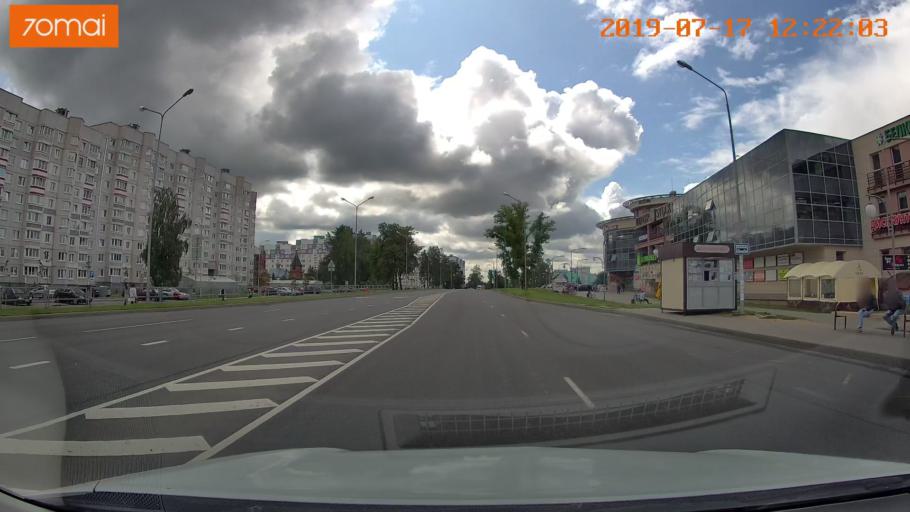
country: BY
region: Minsk
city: Borovlyany
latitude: 54.0043
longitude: 27.6778
